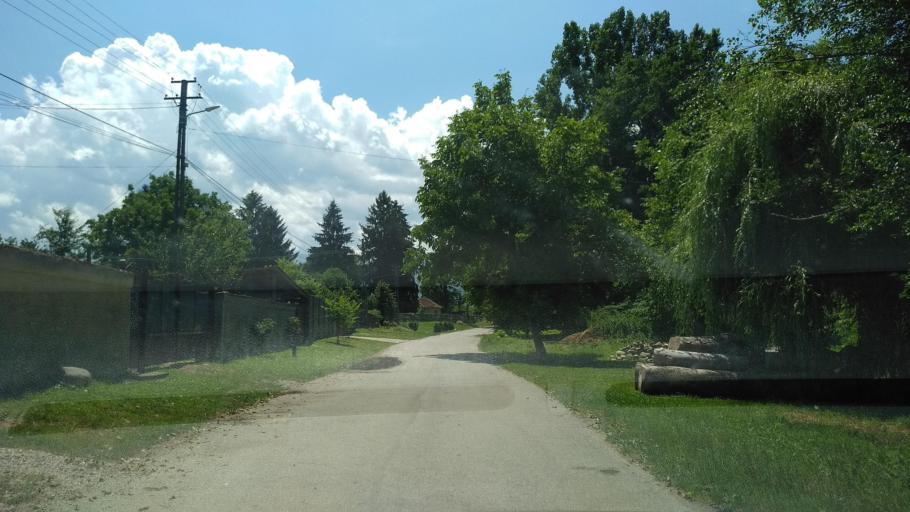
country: RO
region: Hunedoara
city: Densus
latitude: 45.5458
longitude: 22.8210
